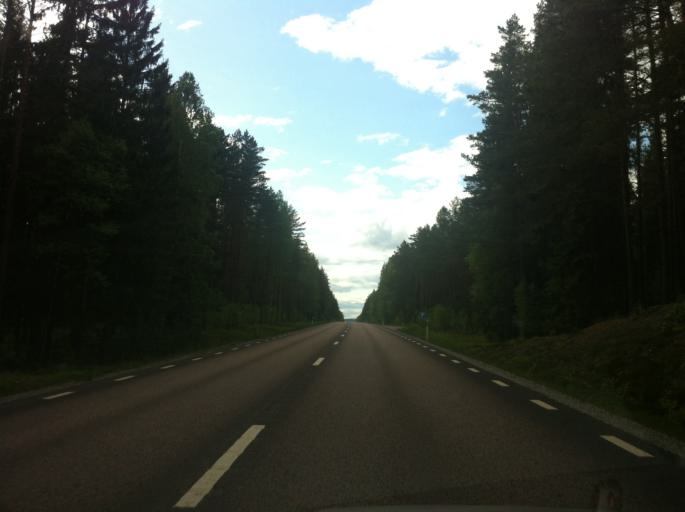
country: SE
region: Vaermland
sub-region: Filipstads Kommun
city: Filipstad
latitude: 59.6477
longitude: 14.2451
